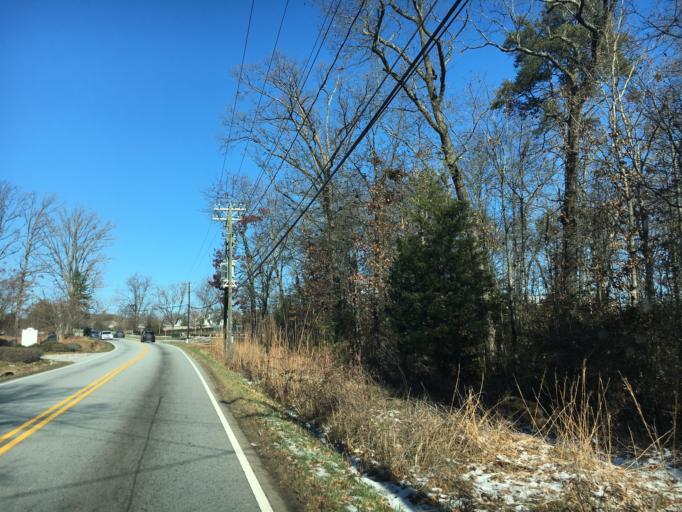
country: US
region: South Carolina
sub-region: Greenville County
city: Taylors
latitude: 34.9314
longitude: -82.2693
